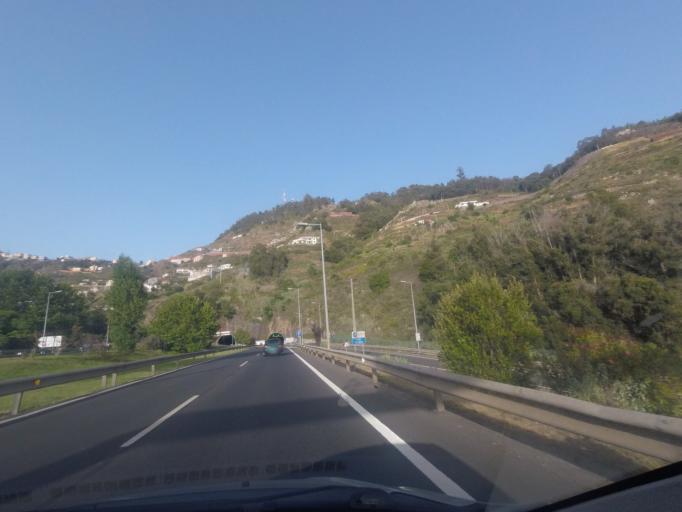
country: PT
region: Madeira
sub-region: Ribeira Brava
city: Campanario
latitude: 32.6587
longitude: -17.0126
